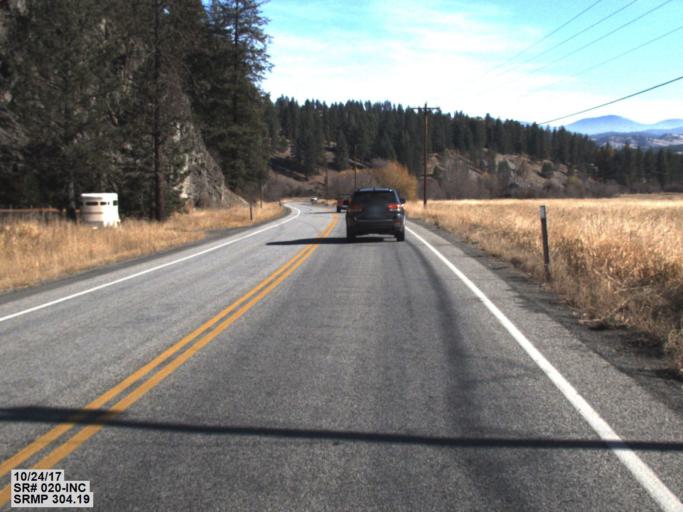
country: US
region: Washington
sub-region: Ferry County
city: Republic
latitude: 48.6513
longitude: -118.7060
